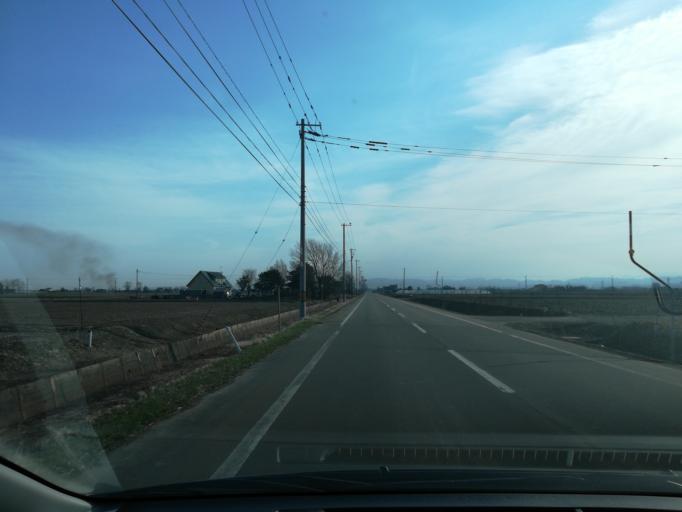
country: JP
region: Hokkaido
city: Iwamizawa
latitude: 43.1818
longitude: 141.6904
